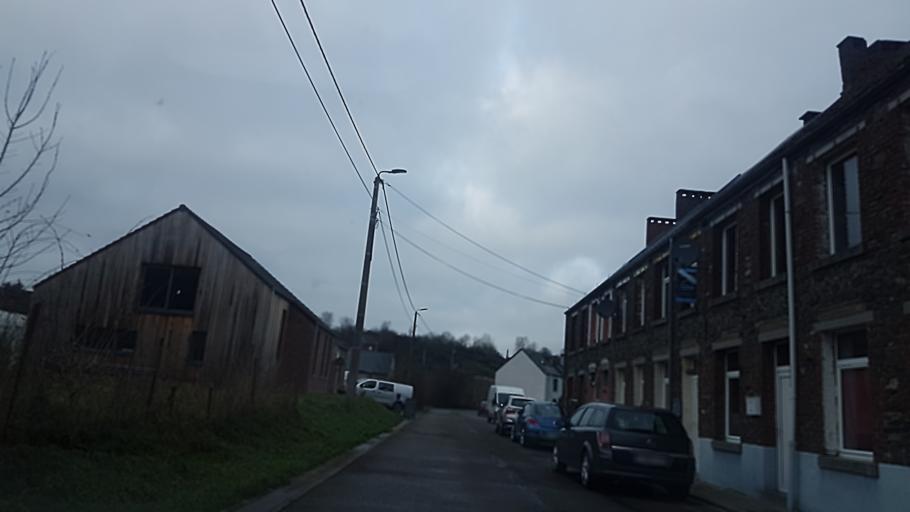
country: FR
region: Champagne-Ardenne
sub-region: Departement des Ardennes
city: Haybes
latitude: 50.0669
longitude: 4.6124
